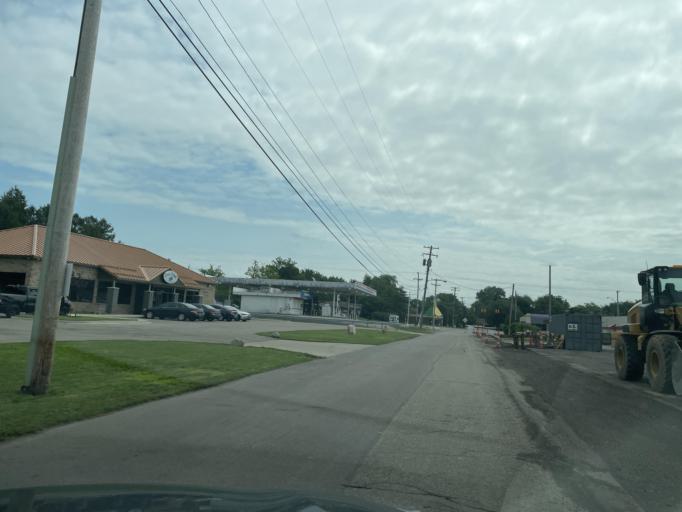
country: US
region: Michigan
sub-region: Kent County
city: Kentwood
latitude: 42.8867
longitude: -85.6279
